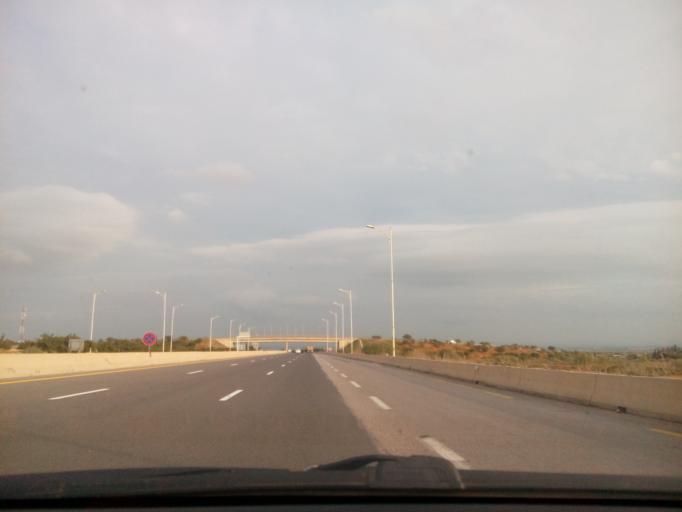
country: DZ
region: Relizane
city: Relizane
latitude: 35.7894
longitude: 0.4077
